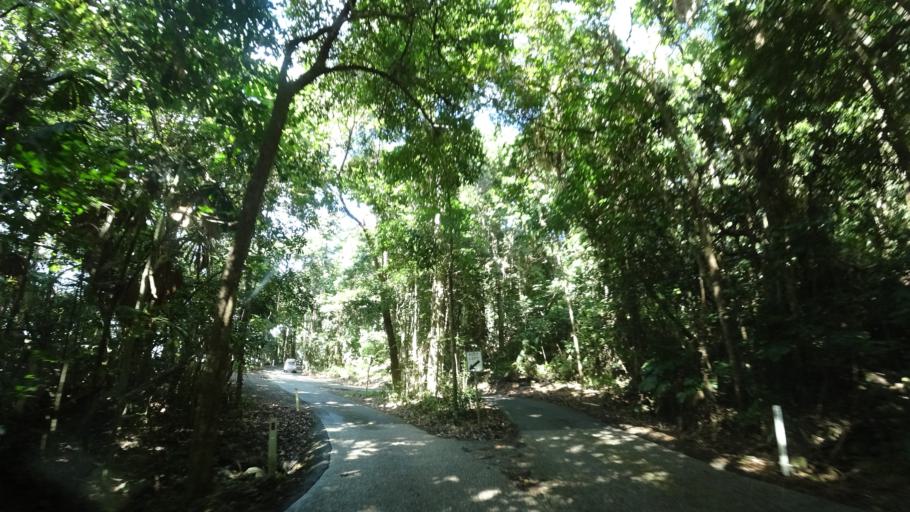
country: AU
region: Queensland
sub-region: Cairns
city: Port Douglas
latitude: -16.1130
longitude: 145.4570
